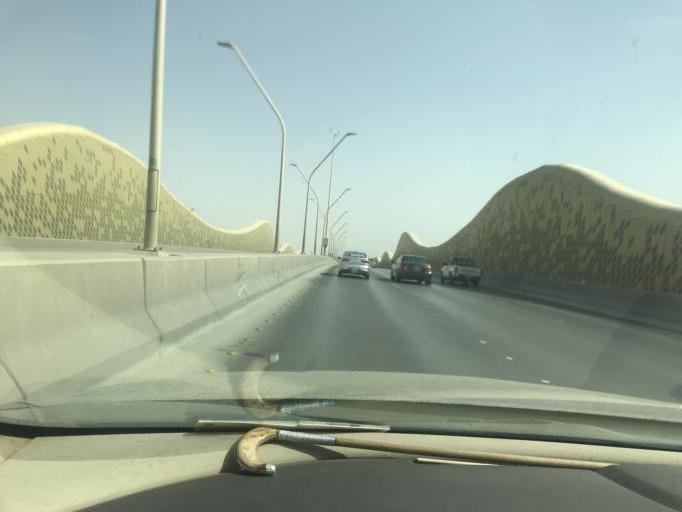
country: SA
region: Ar Riyad
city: Riyadh
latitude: 24.7617
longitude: 46.6943
